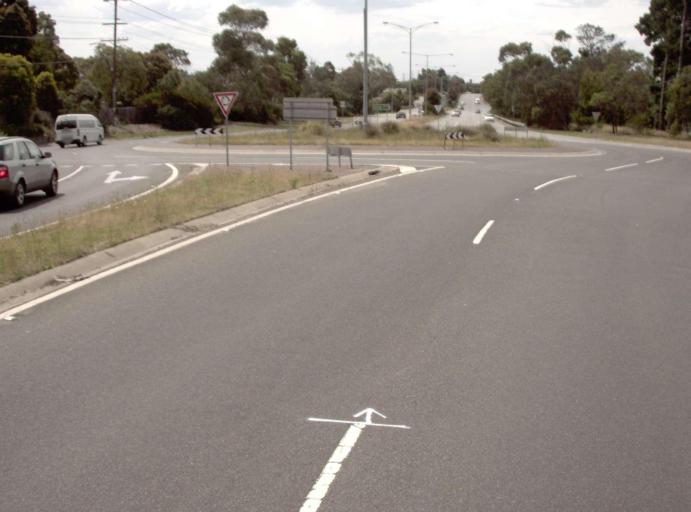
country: AU
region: Victoria
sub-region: Frankston
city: Frankston South
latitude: -38.1830
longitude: 145.1402
